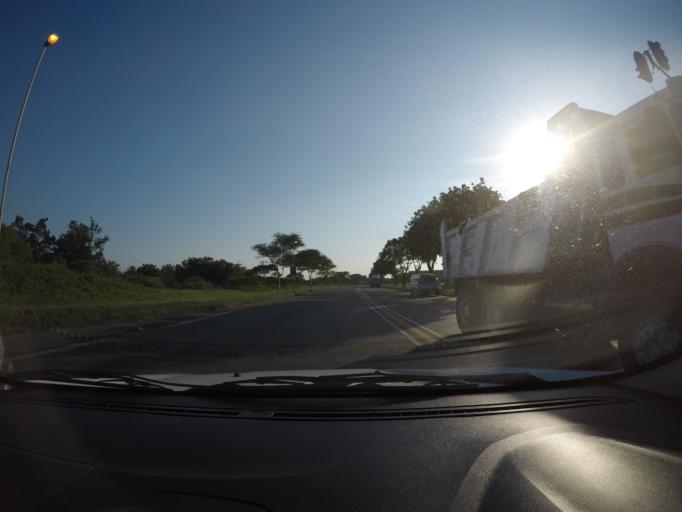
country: ZA
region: KwaZulu-Natal
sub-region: uThungulu District Municipality
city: Richards Bay
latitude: -28.7624
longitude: 32.0211
